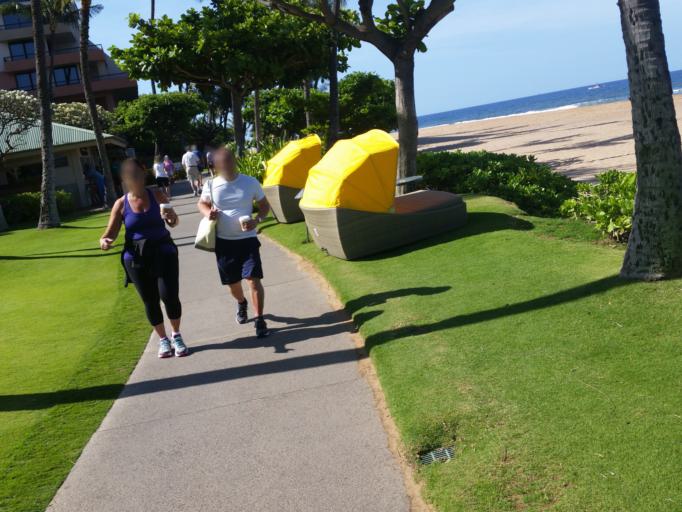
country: US
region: Hawaii
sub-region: Maui County
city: Ka'anapali
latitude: 20.9169
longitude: -156.6964
